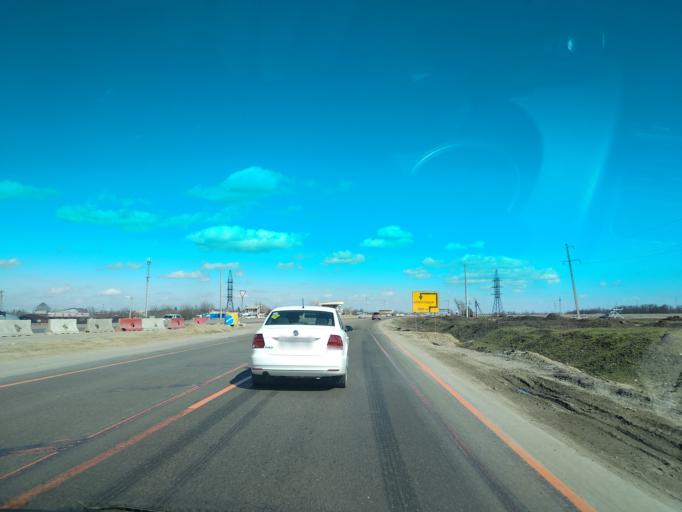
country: RU
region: Krasnodarskiy
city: Agronom
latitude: 45.1807
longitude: 39.1122
